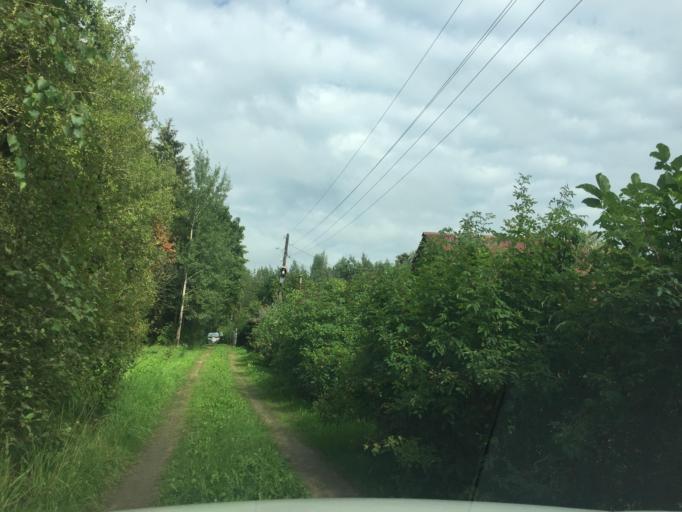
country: RU
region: Leningrad
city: Siverskiy
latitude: 59.2972
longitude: 30.0240
